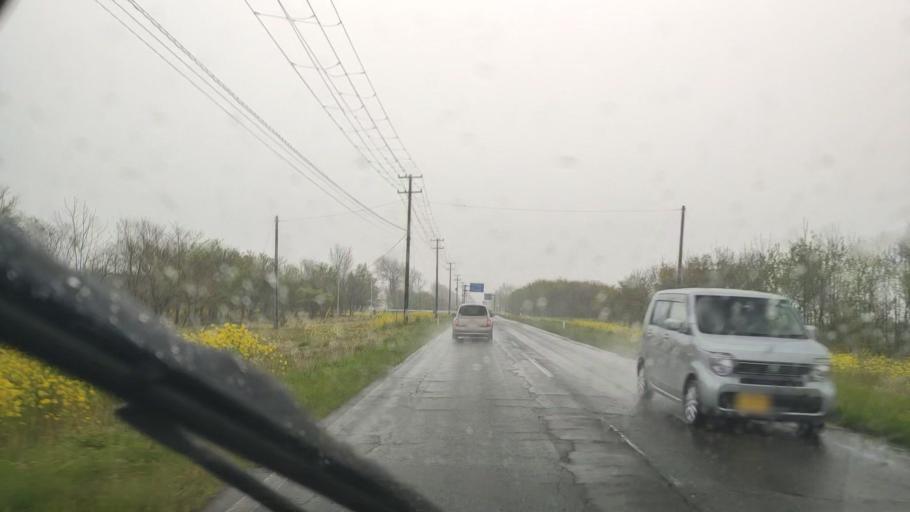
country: JP
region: Akita
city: Tenno
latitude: 39.9934
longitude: 139.9463
